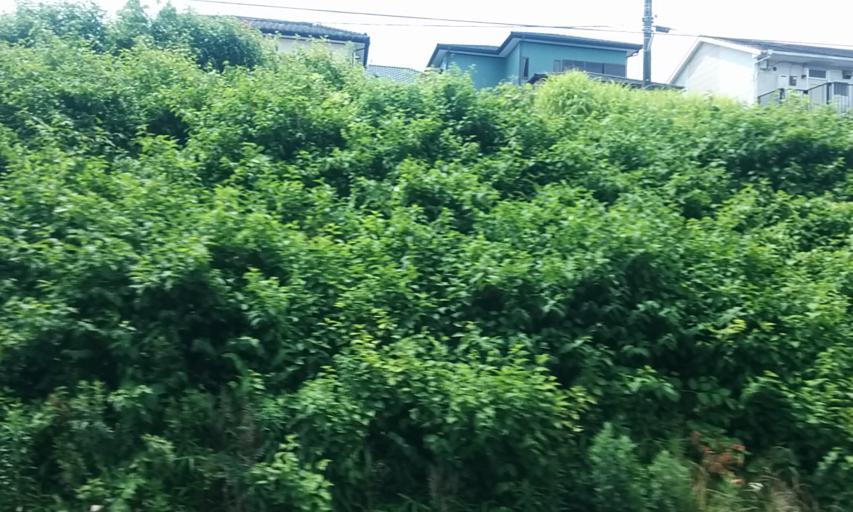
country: JP
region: Chiba
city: Sakura
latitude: 35.7257
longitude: 140.1735
